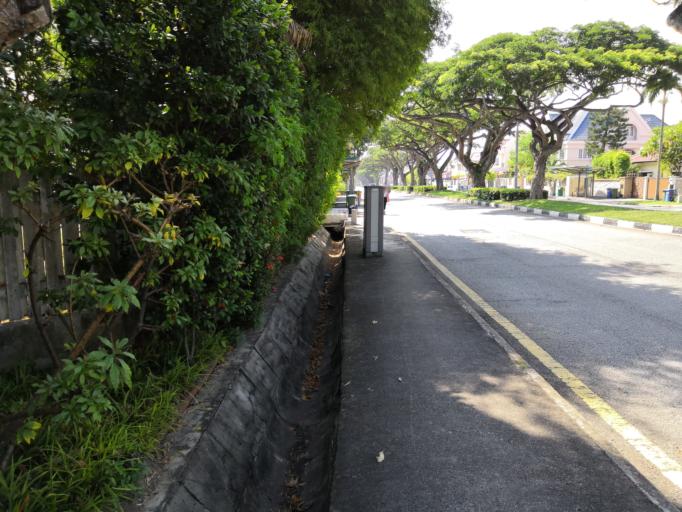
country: SG
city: Singapore
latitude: 1.3124
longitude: 103.9200
